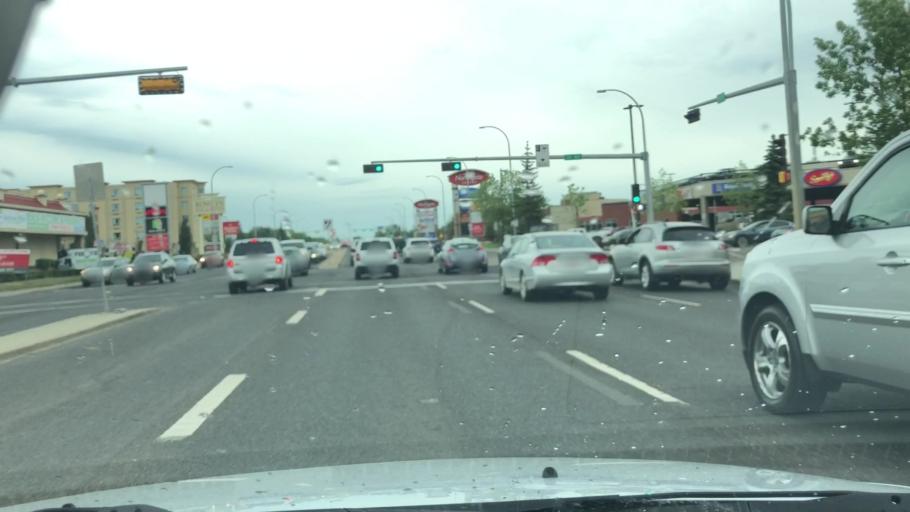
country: CA
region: Alberta
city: Edmonton
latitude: 53.5965
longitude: -113.4919
